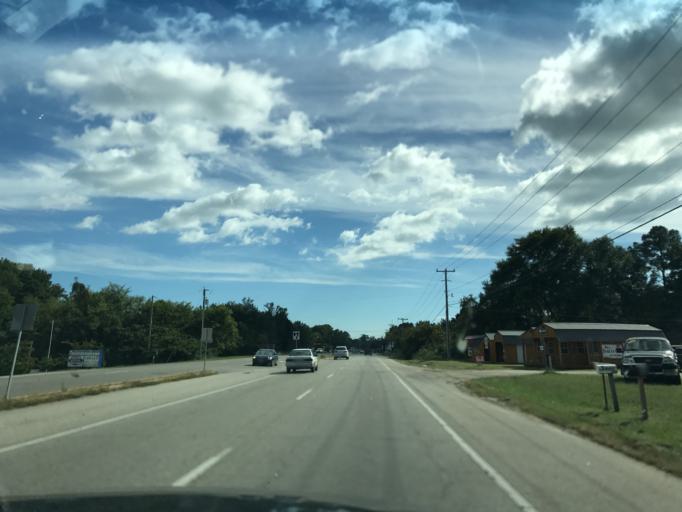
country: US
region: Virginia
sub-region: Gloucester County
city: Gloucester Point
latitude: 37.3104
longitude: -76.5132
